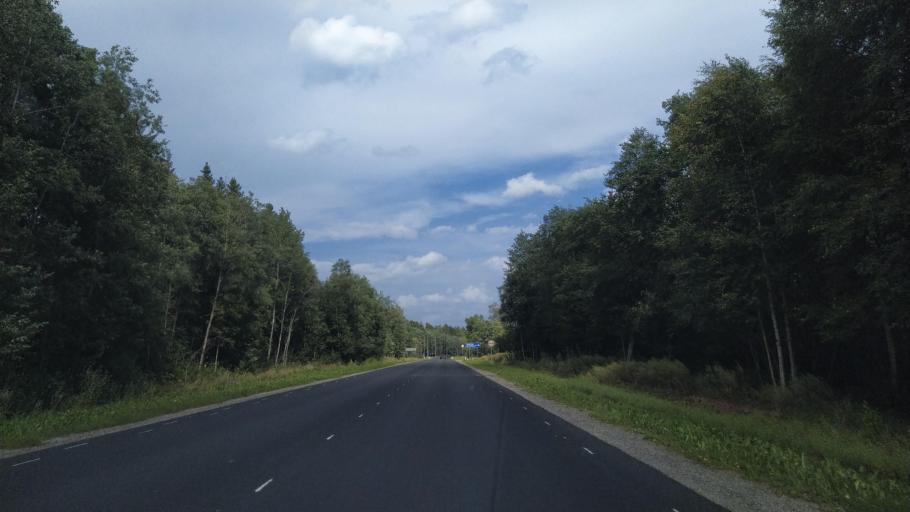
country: RU
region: Pskov
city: Vybor
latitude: 57.7249
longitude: 28.9585
